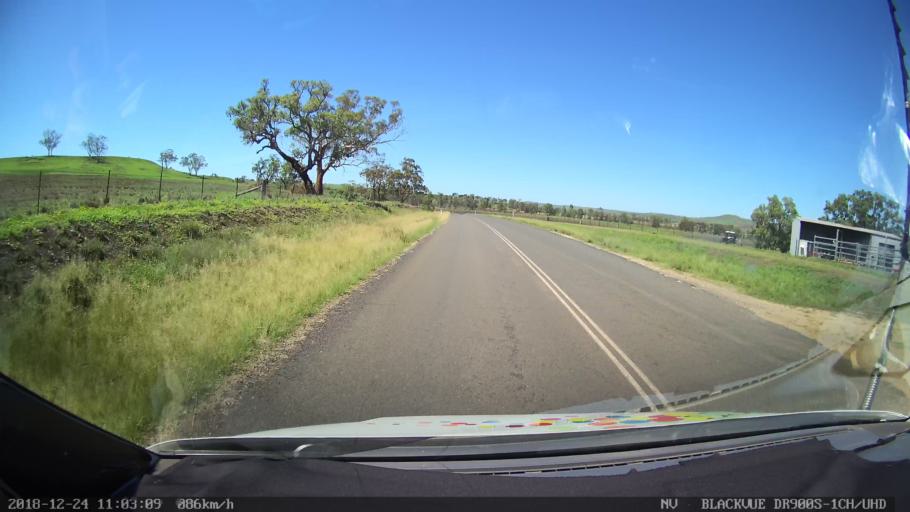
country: AU
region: New South Wales
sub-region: Upper Hunter Shire
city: Merriwa
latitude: -32.0932
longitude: 150.3694
